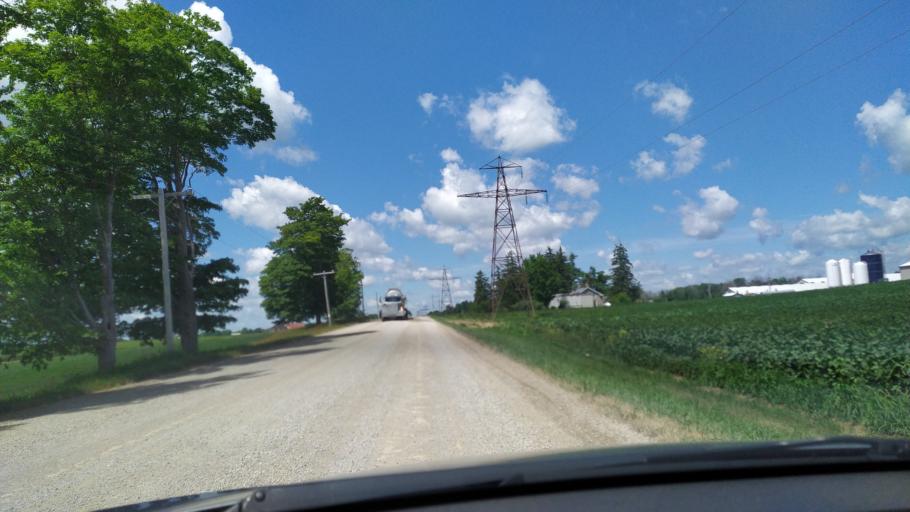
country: CA
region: Ontario
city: Stratford
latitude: 43.3878
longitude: -80.8155
